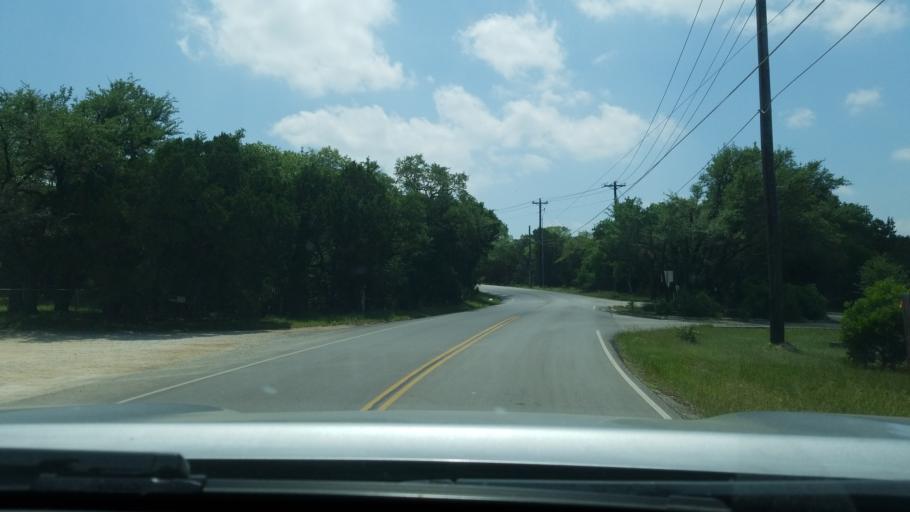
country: US
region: Texas
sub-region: Hays County
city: Woodcreek
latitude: 30.0262
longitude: -98.1295
